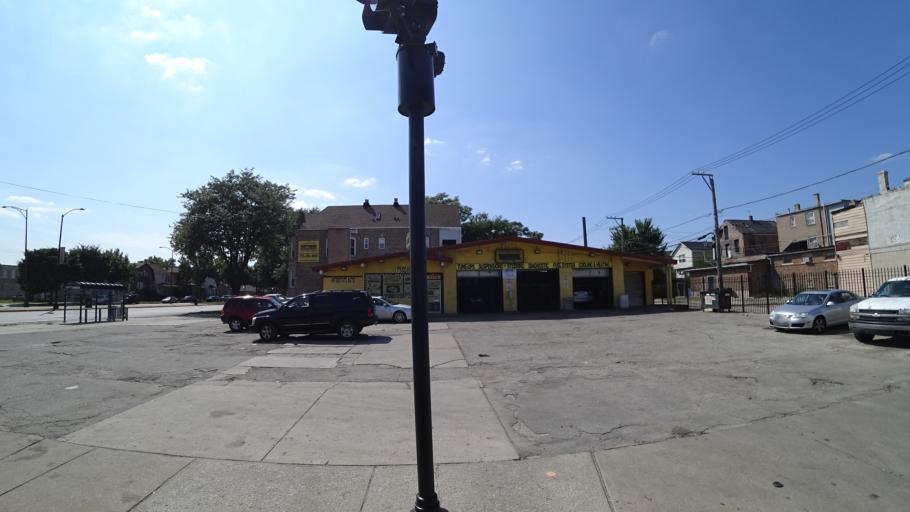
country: US
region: Illinois
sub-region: Cook County
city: Cicero
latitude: 41.8520
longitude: -87.7248
